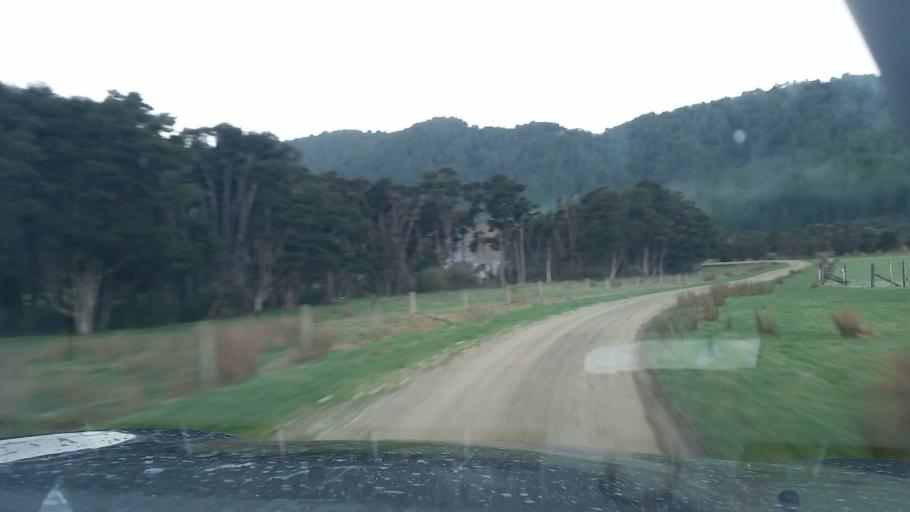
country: NZ
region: Marlborough
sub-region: Marlborough District
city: Picton
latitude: -41.1575
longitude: 174.1323
